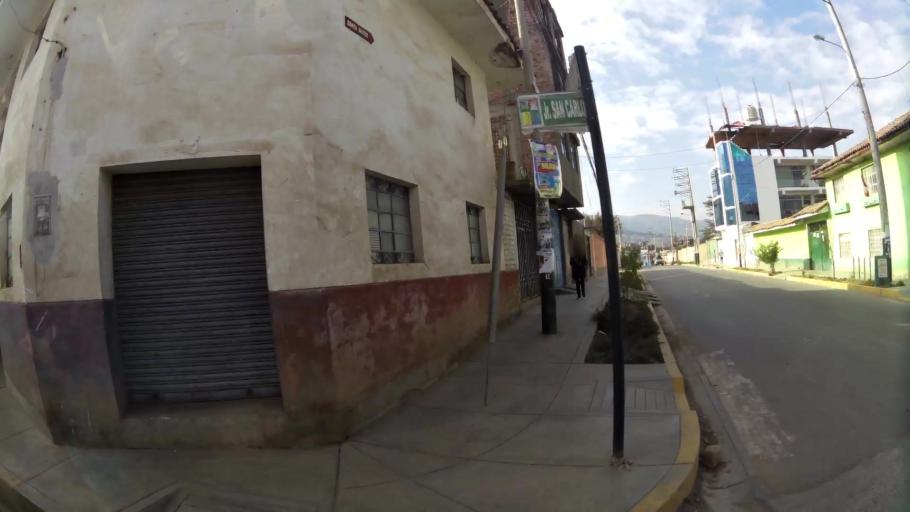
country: PE
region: Junin
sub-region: Provincia de Huancayo
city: Huancayo
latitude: -12.0461
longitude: -75.1983
